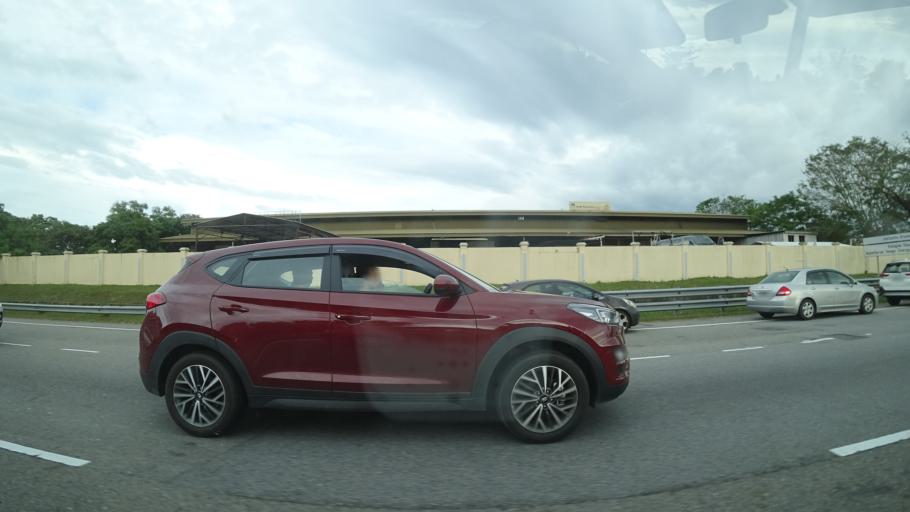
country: BN
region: Brunei and Muara
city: Bandar Seri Begawan
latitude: 4.8935
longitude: 114.8988
